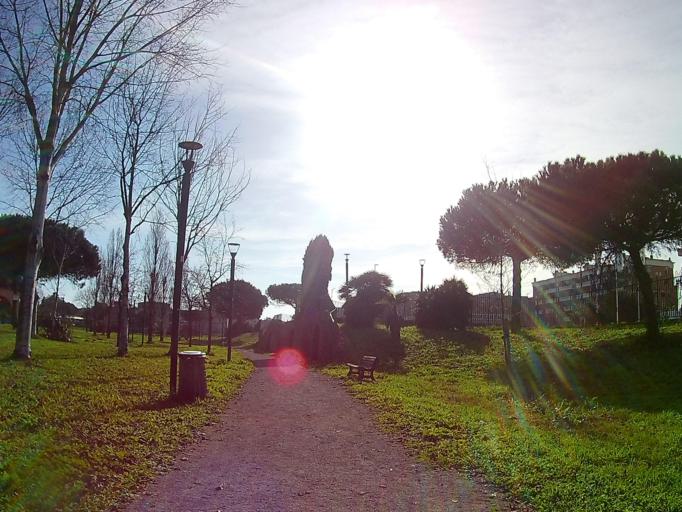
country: IT
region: Latium
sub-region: Citta metropolitana di Roma Capitale
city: Lido di Ostia
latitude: 41.7416
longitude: 12.2611
